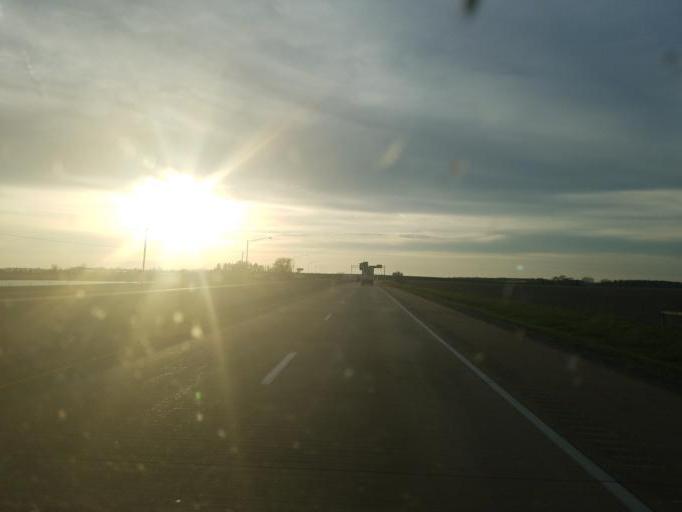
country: US
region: Ohio
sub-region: Wood County
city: Luckey
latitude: 41.4840
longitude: -83.4447
